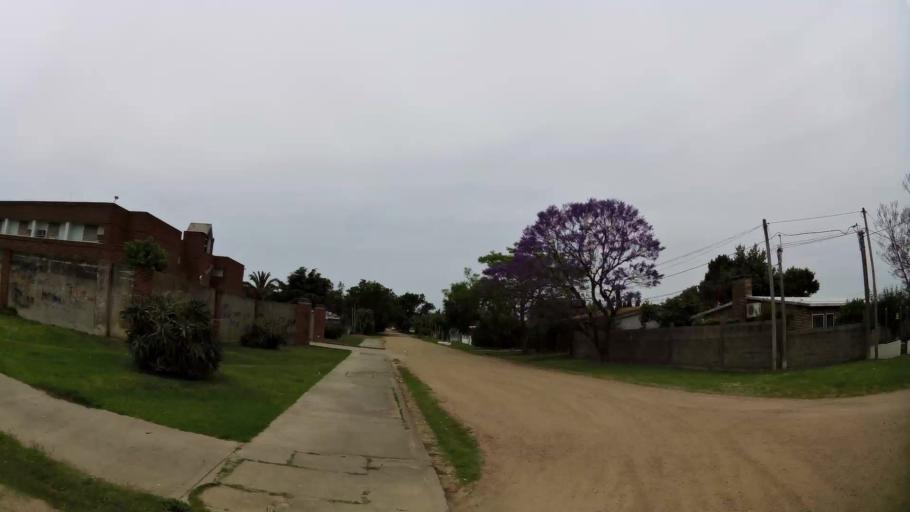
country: UY
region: Canelones
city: La Paz
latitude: -34.7508
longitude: -56.2269
